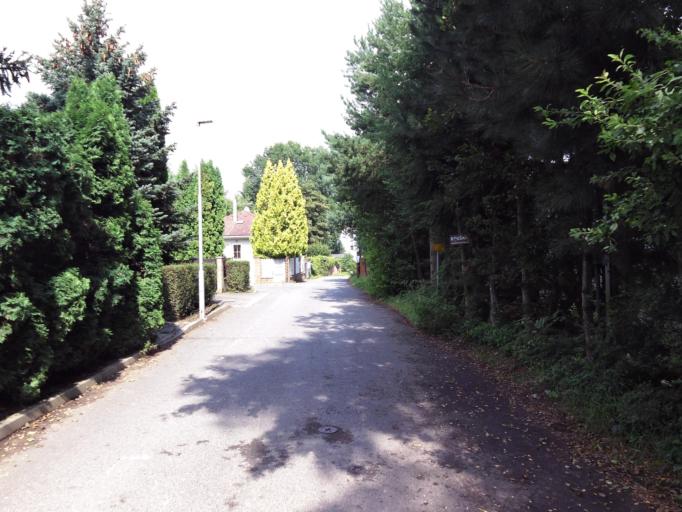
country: CZ
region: Central Bohemia
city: Jesenice
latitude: 49.9716
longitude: 14.5416
